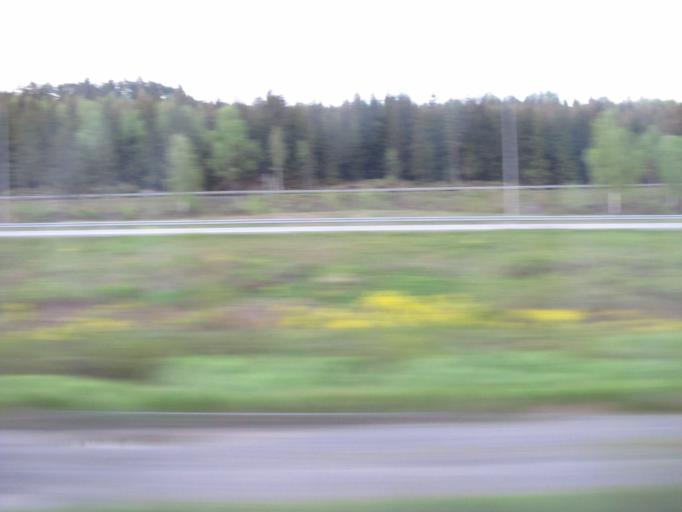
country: NO
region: Oppland
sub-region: Lillehammer
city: Lillehammer
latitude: 61.2114
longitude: 10.4362
